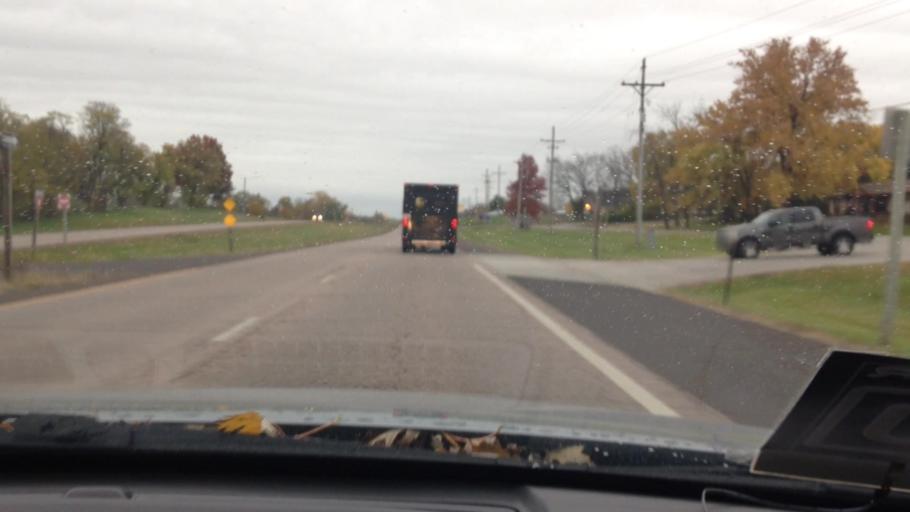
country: US
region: Kansas
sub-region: Leavenworth County
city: Lansing
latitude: 39.2076
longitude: -94.9005
